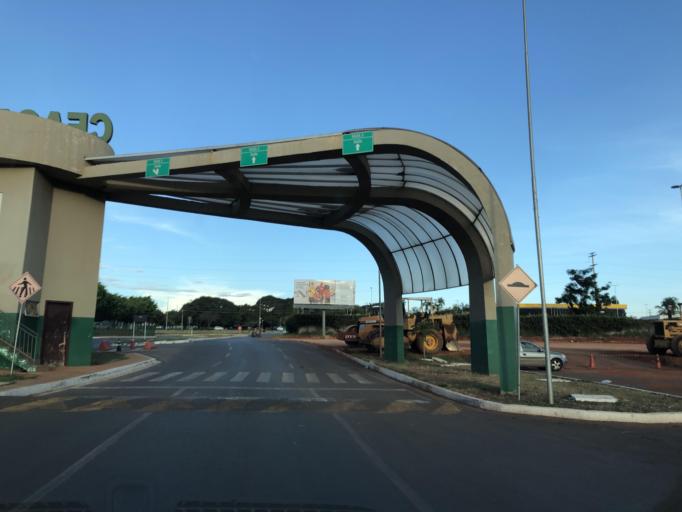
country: BR
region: Federal District
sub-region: Brasilia
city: Brasilia
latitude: -15.7918
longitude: -47.9459
